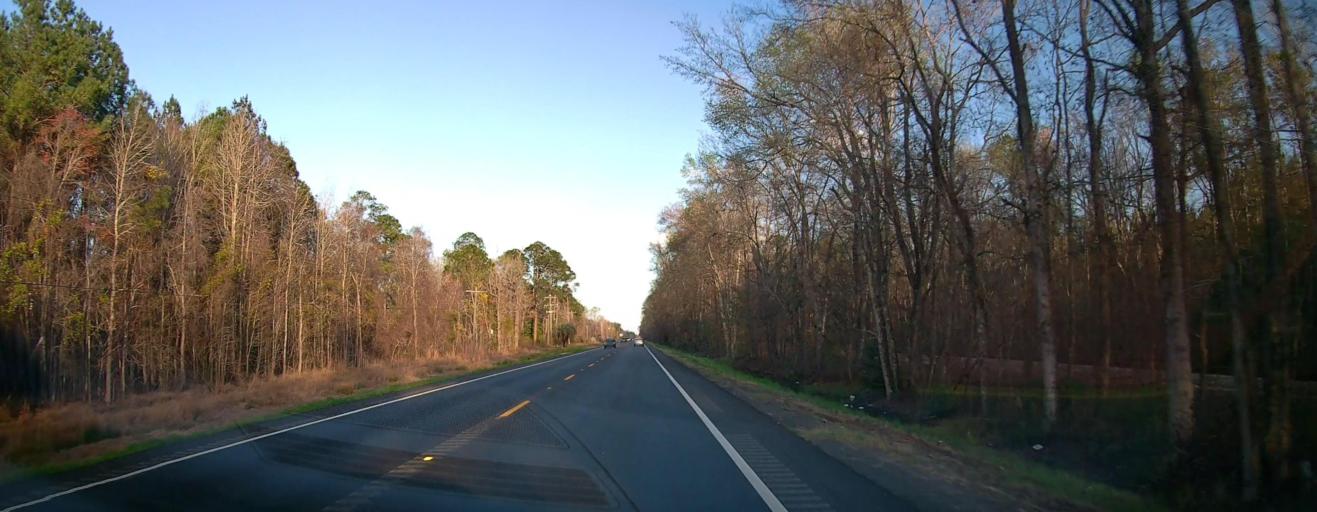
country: US
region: Georgia
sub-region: Bryan County
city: Pembroke
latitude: 32.1343
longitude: -81.6018
